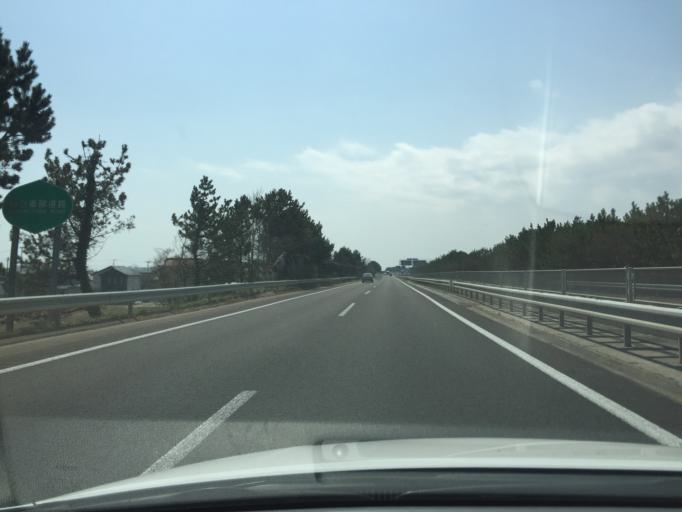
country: JP
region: Miyagi
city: Sendai
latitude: 38.2031
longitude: 140.9434
